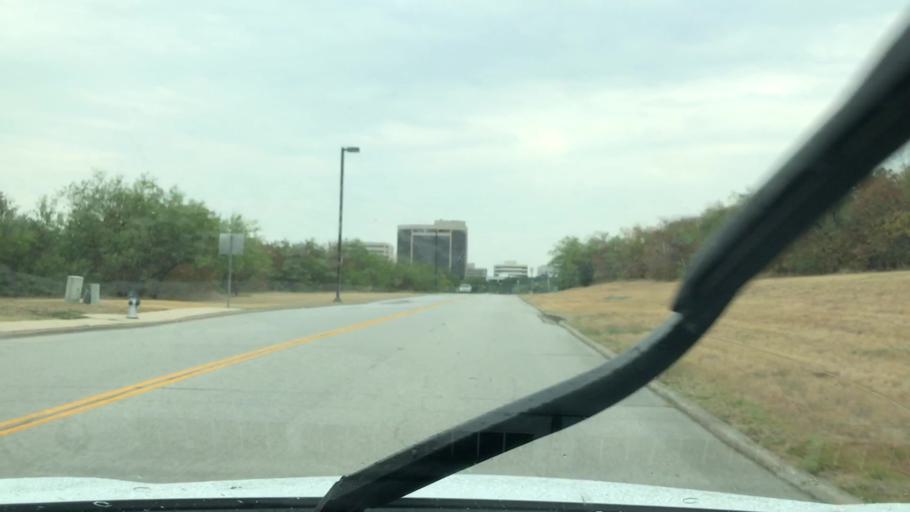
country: US
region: Texas
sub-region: Dallas County
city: Coppell
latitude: 32.8884
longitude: -96.9778
